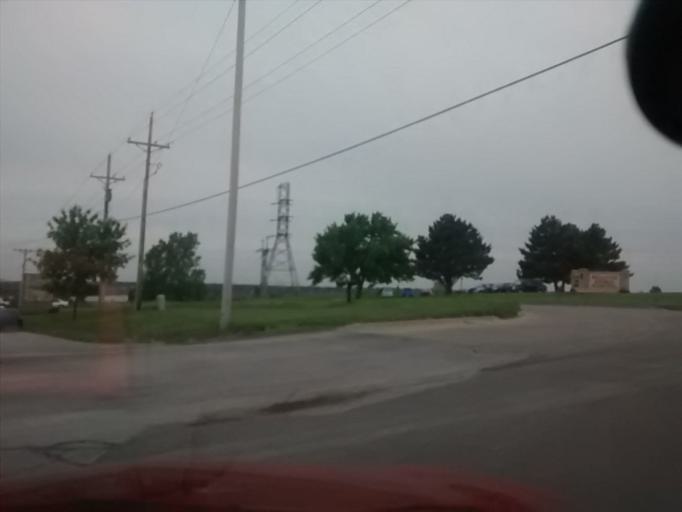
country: US
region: Nebraska
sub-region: Sarpy County
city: Offutt Air Force Base
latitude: 41.1584
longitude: -95.9473
